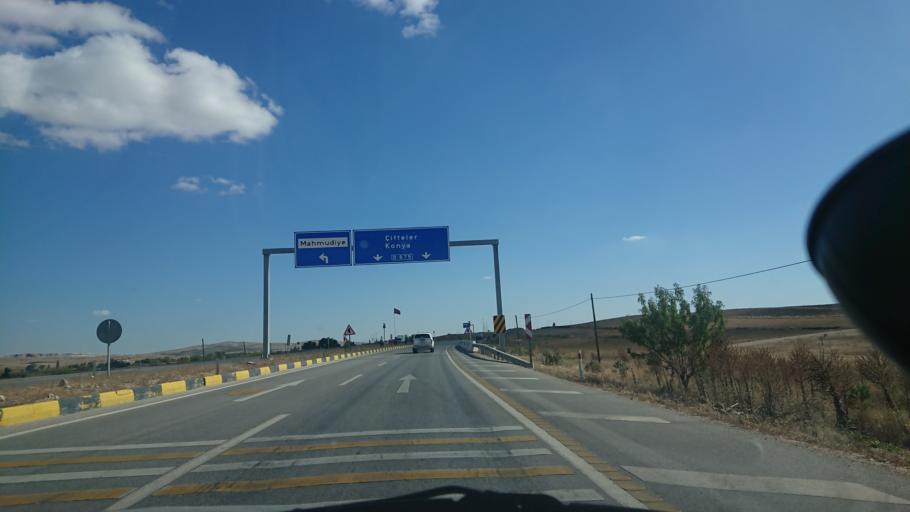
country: TR
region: Eskisehir
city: Mahmudiye
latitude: 39.5203
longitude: 30.9602
